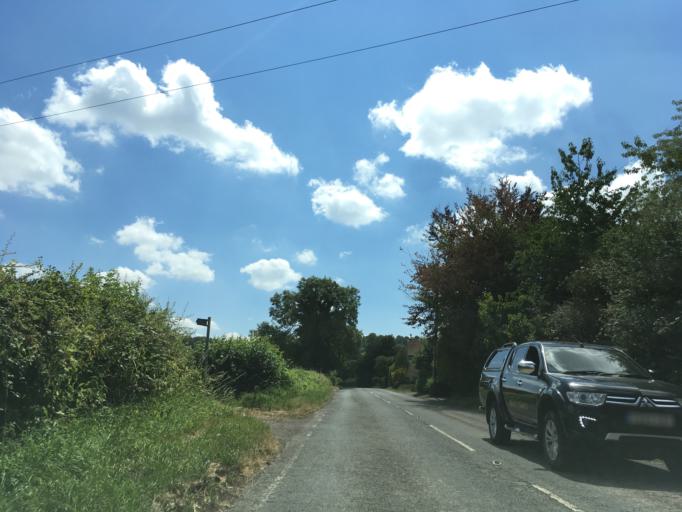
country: GB
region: England
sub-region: Gloucestershire
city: Painswick
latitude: 51.8208
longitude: -2.2084
